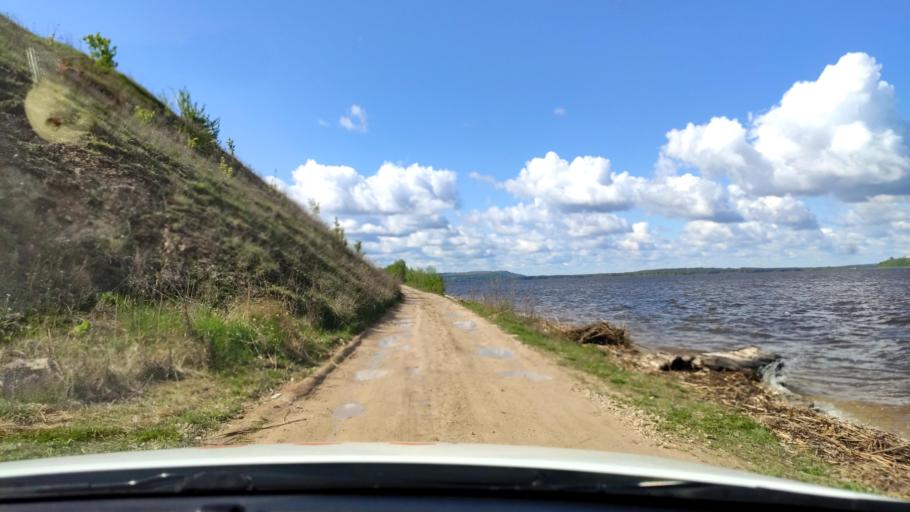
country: RU
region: Tatarstan
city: Sviyazhsk
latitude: 55.7773
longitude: 48.6923
